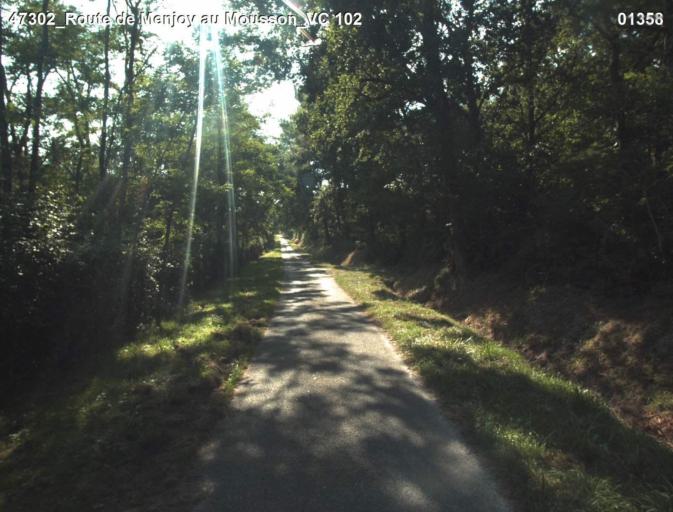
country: FR
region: Aquitaine
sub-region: Departement du Lot-et-Garonne
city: Mezin
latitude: 44.0534
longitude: 0.1801
